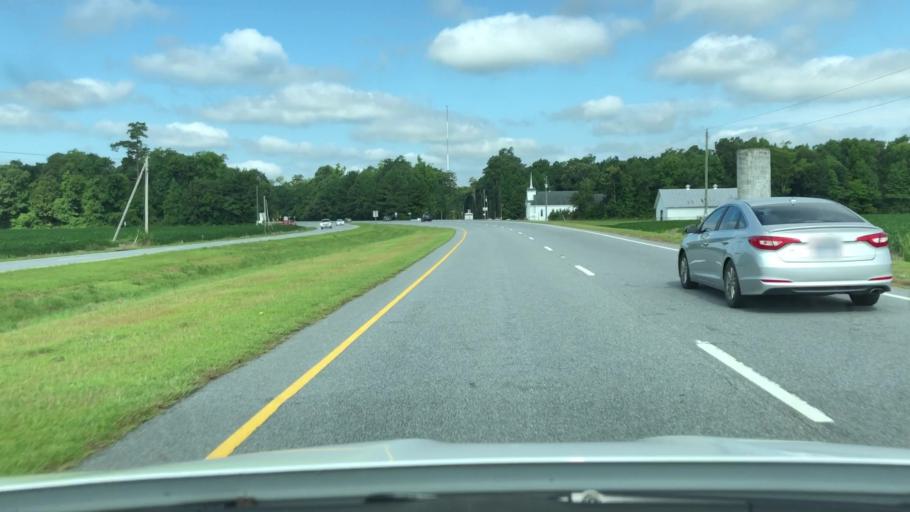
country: US
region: North Carolina
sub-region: Perquimans County
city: Hertford
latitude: 36.2125
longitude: -76.4287
